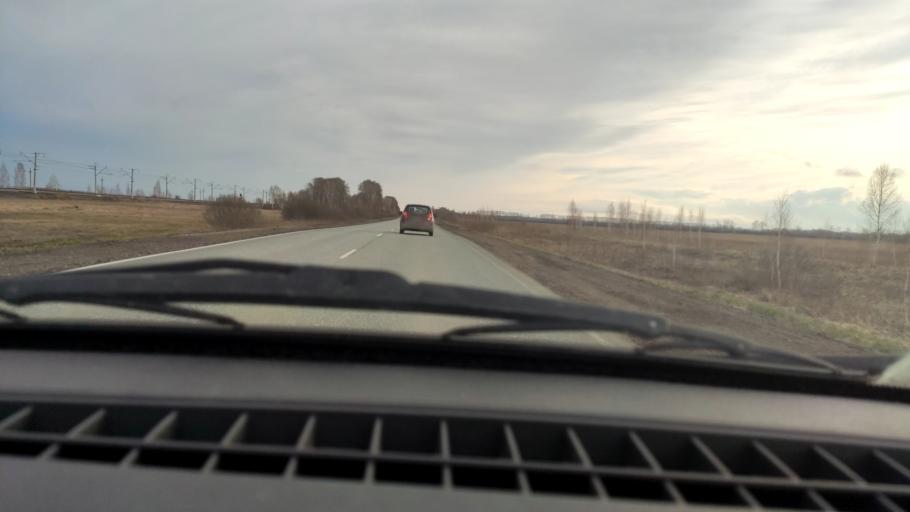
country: RU
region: Bashkortostan
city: Chishmy
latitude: 54.4222
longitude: 55.2292
